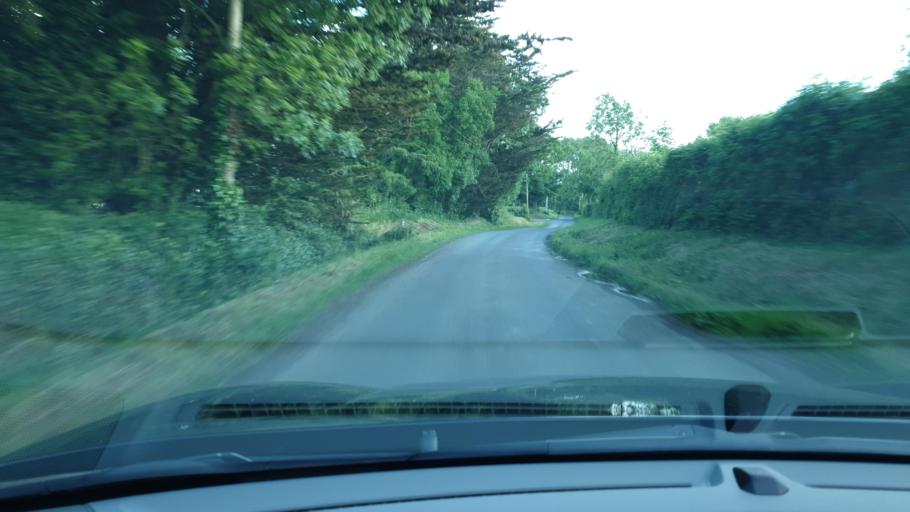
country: IE
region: Leinster
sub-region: An Mhi
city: Ashbourne
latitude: 53.4767
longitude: -6.3540
